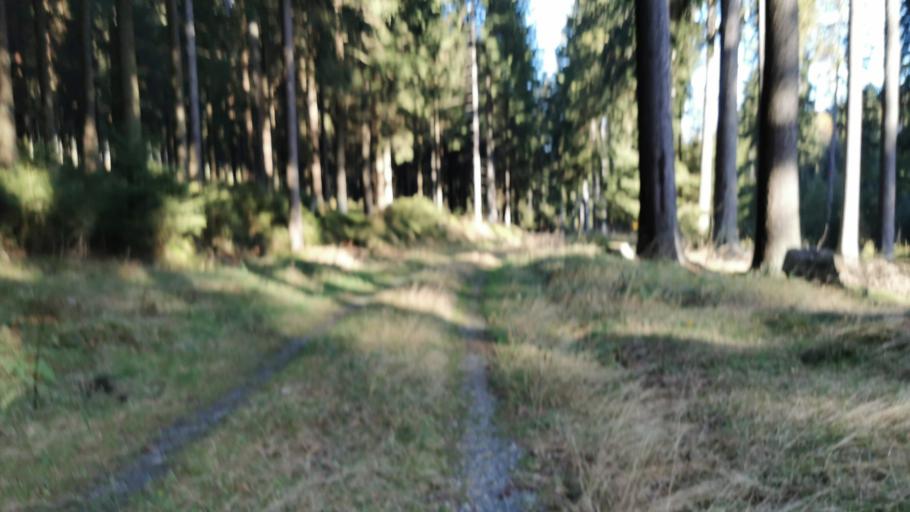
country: DE
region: Bavaria
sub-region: Upper Franconia
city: Reichenbach
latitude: 50.4452
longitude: 11.4278
